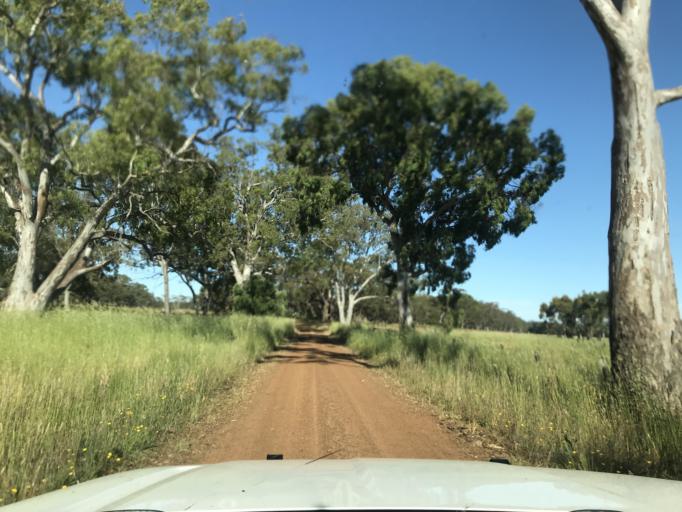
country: AU
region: South Australia
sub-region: Wattle Range
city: Penola
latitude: -37.0838
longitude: 141.3639
